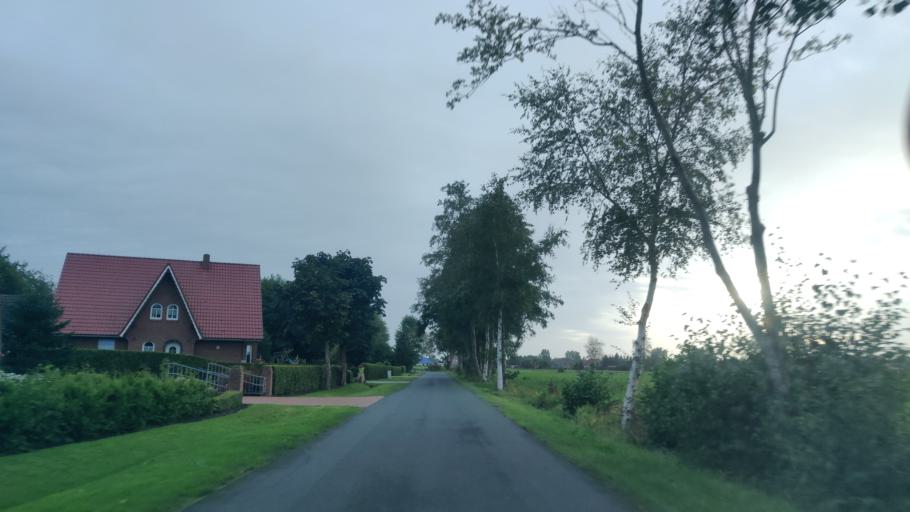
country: DE
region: Lower Saxony
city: Rechtsupweg
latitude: 53.4862
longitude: 7.3941
